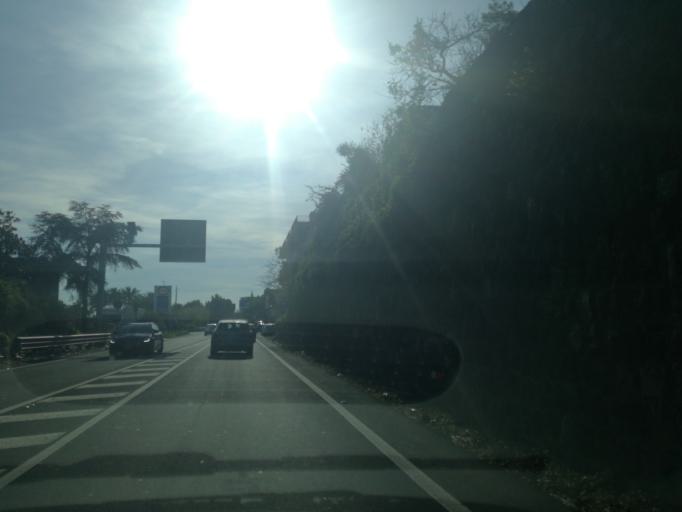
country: IT
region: Sicily
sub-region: Catania
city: Acireale
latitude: 37.6022
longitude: 15.1684
